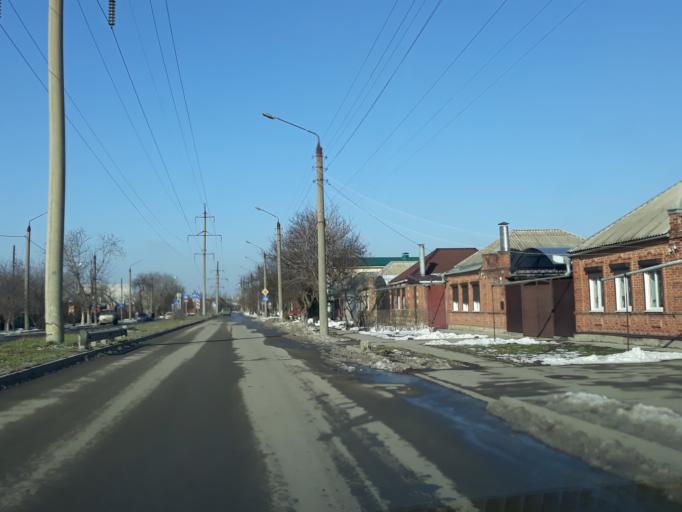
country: RU
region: Rostov
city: Taganrog
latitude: 47.2193
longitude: 38.8801
